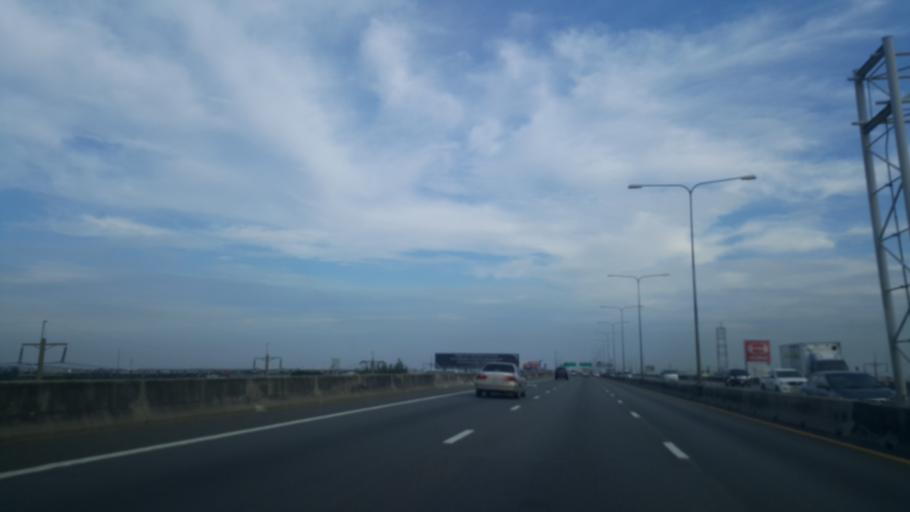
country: TH
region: Bangkok
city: Bang Na
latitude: 13.6262
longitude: 100.7258
